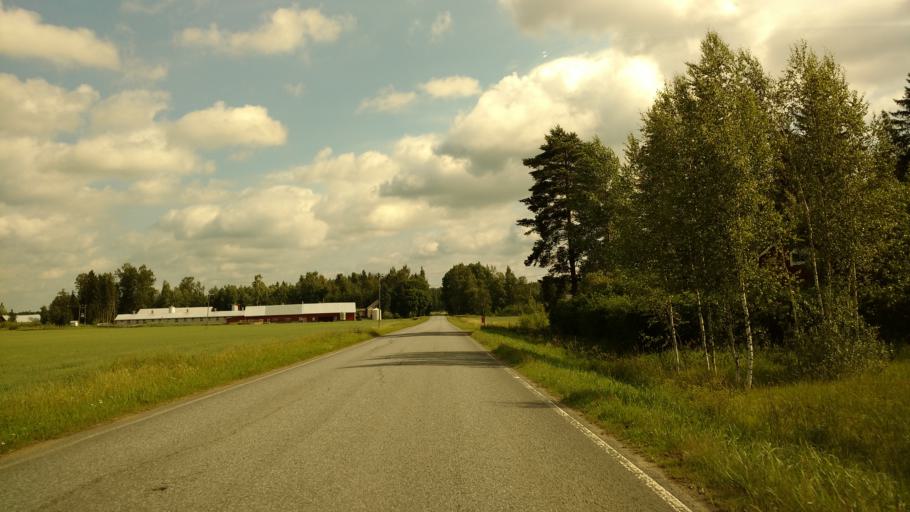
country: FI
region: Haeme
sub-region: Forssa
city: Ypaejae
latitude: 60.7614
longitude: 23.2126
